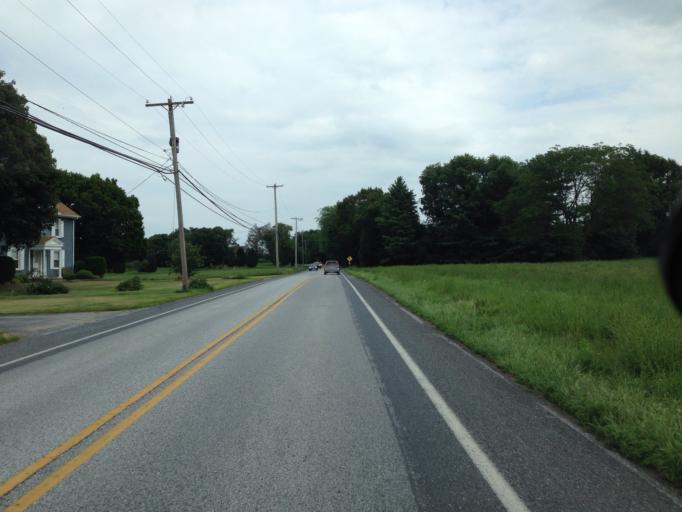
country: US
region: Delaware
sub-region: New Castle County
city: Newark
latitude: 39.7398
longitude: -75.7997
